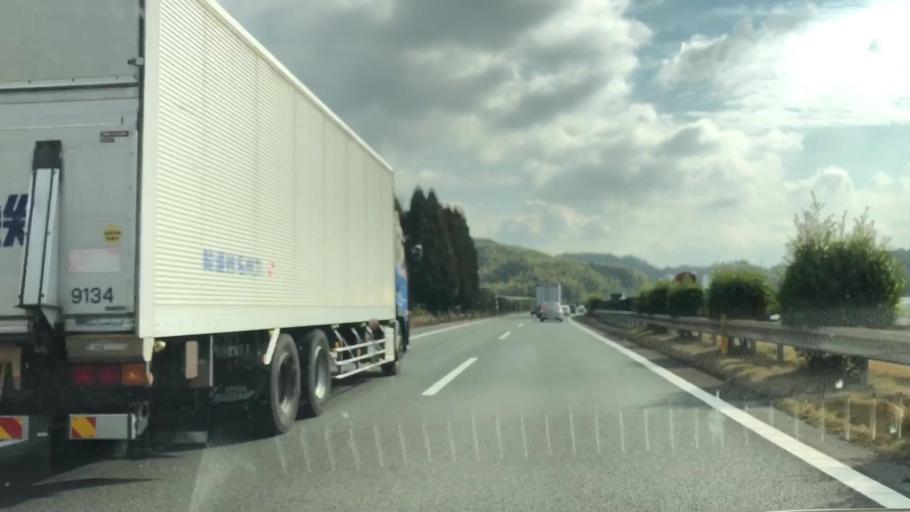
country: JP
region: Fukuoka
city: Setakamachi-takayanagi
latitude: 33.0873
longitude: 130.5404
